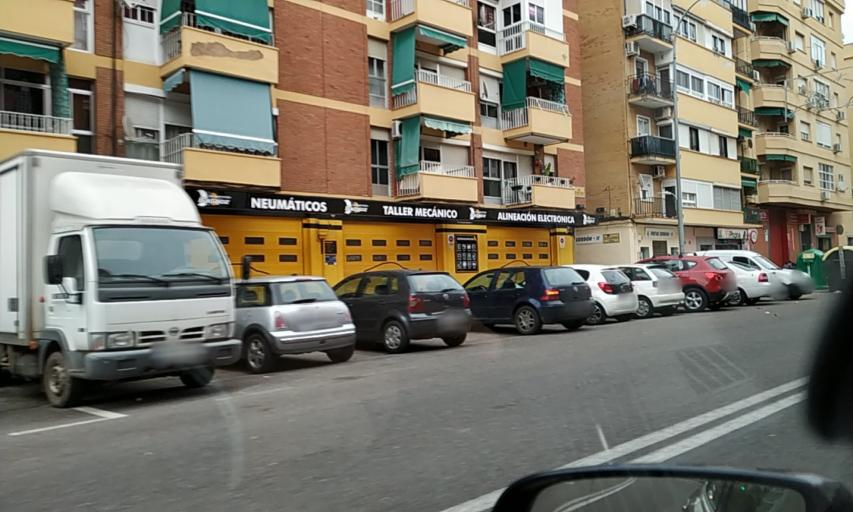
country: ES
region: Extremadura
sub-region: Provincia de Badajoz
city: Badajoz
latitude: 38.8789
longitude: -6.9548
